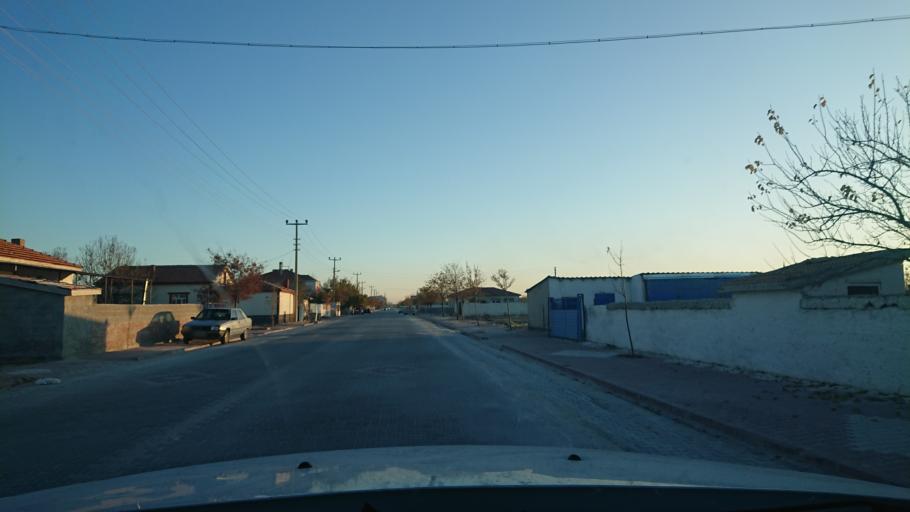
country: TR
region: Aksaray
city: Eskil
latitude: 38.4016
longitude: 33.4202
